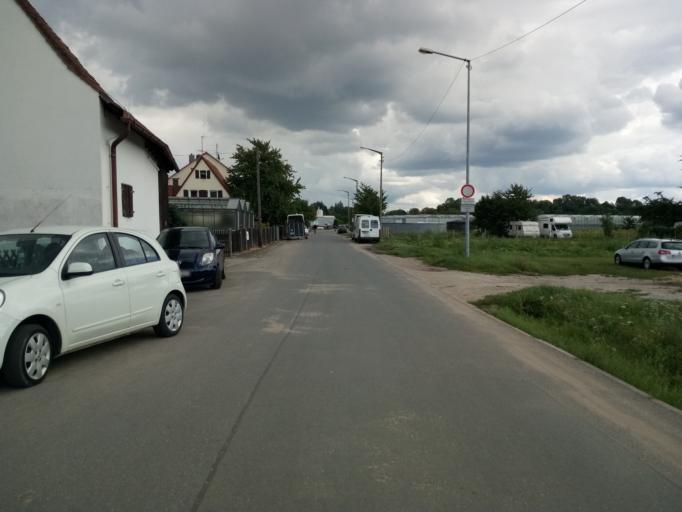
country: DE
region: Bavaria
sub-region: Regierungsbezirk Mittelfranken
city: Nuernberg
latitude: 49.4868
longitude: 11.0765
